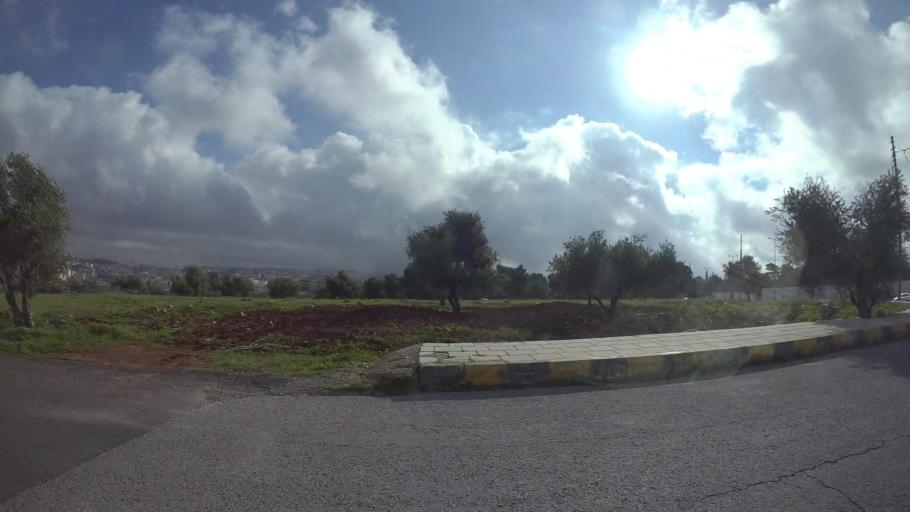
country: JO
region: Amman
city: Al Jubayhah
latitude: 32.0400
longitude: 35.8675
